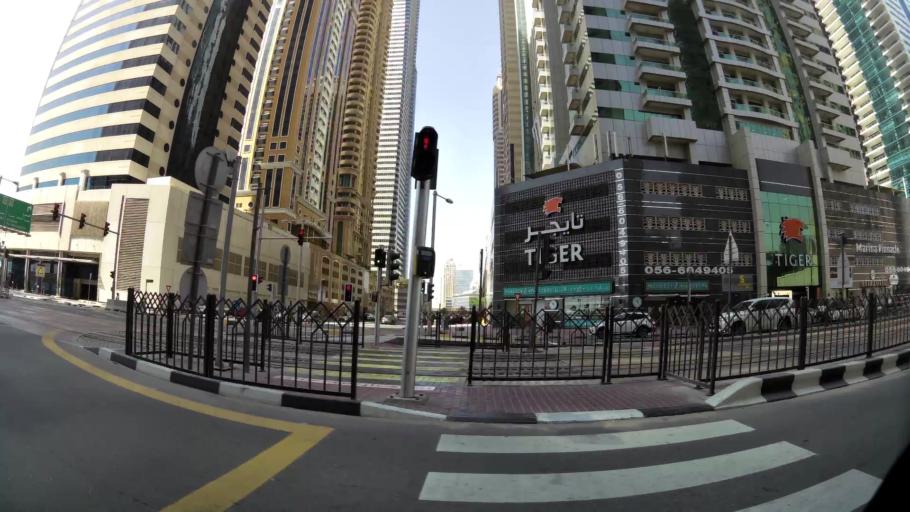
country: AE
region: Dubai
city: Dubai
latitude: 25.0884
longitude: 55.1477
